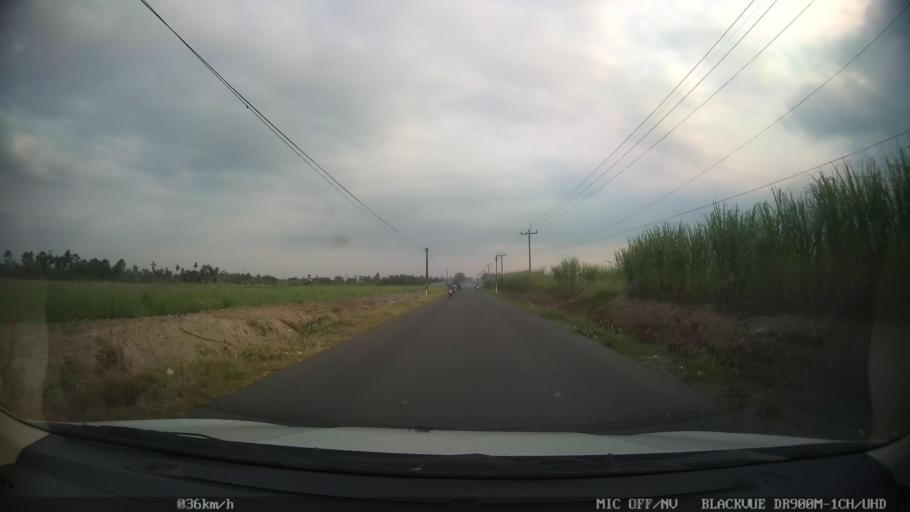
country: ID
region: North Sumatra
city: Sunggal
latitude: 3.5751
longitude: 98.5512
